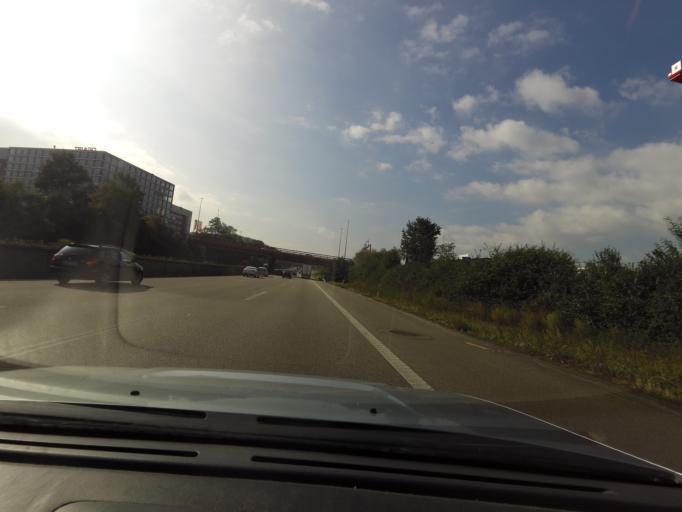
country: CH
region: Basel-Landschaft
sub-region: Bezirk Liestal
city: Pratteln
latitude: 47.5290
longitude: 7.6887
